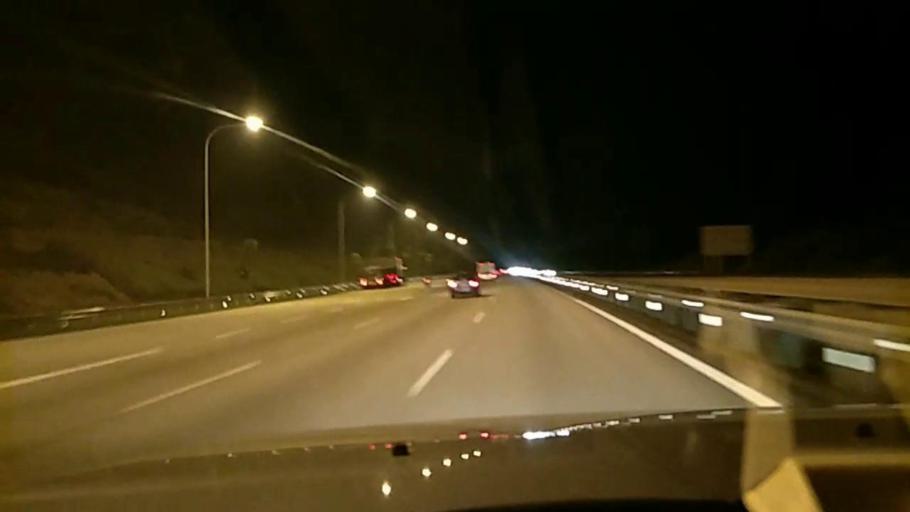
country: MY
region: Selangor
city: Serendah
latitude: 3.3768
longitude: 101.5605
